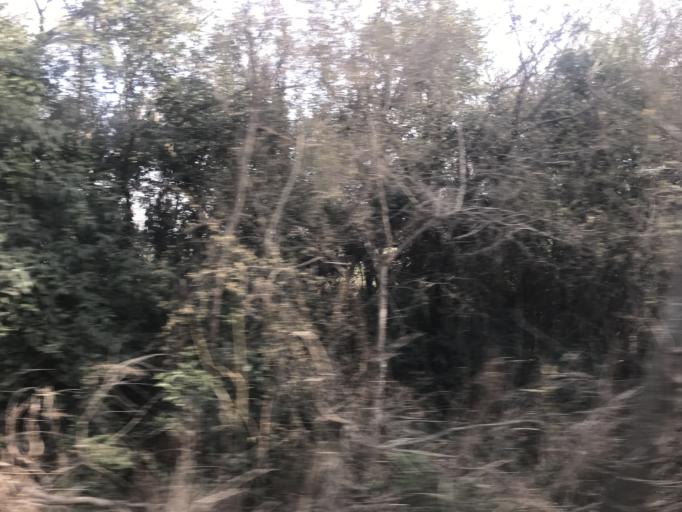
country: AR
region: Cordoba
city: Laguna Larga
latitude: -31.7984
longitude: -63.7842
